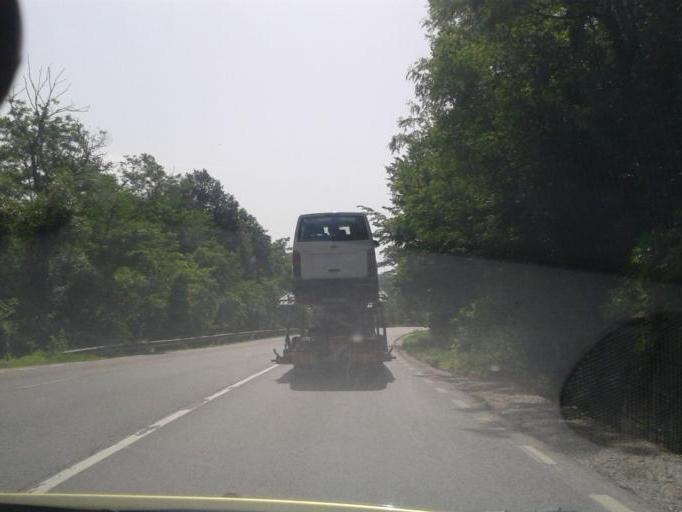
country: RO
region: Arges
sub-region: Comuna Cotmeana
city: Cotmeana
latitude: 44.9698
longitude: 24.6721
